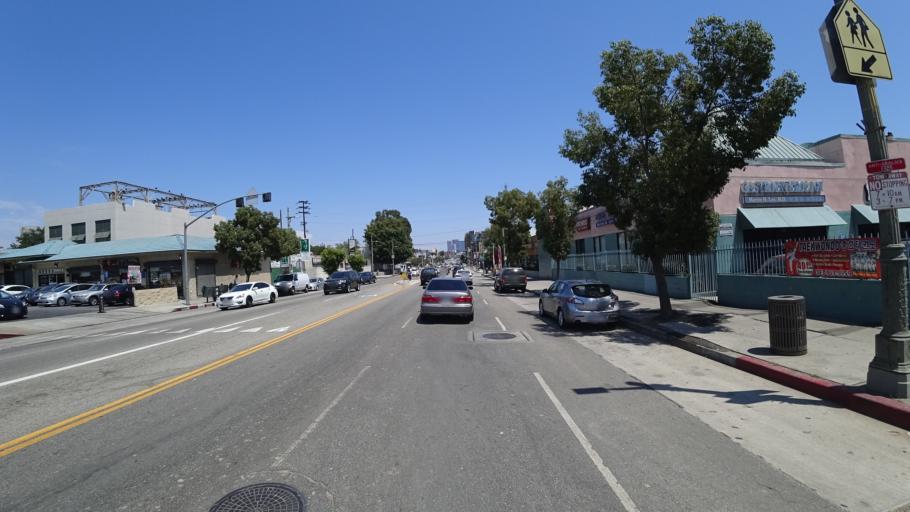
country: US
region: California
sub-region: Los Angeles County
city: Silver Lake
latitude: 34.0526
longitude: -118.3063
